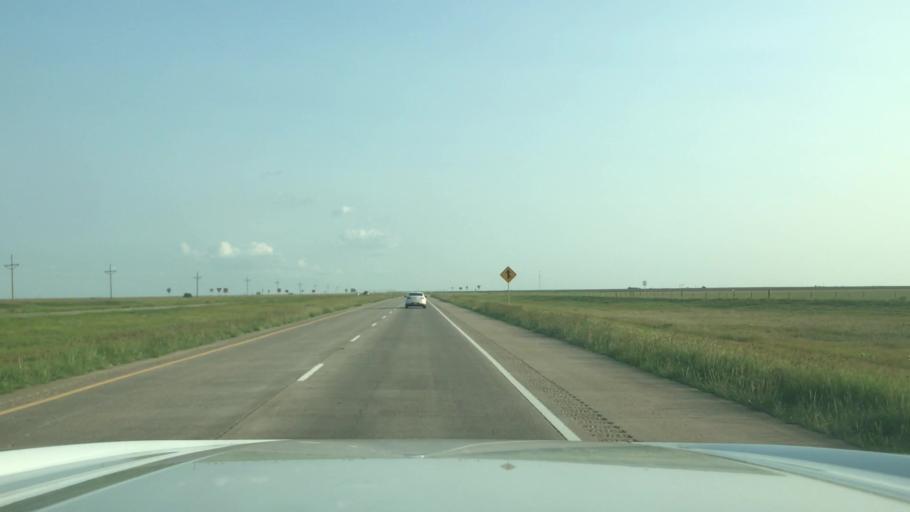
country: US
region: Texas
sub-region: Randall County
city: Canyon
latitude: 34.8803
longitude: -101.8489
